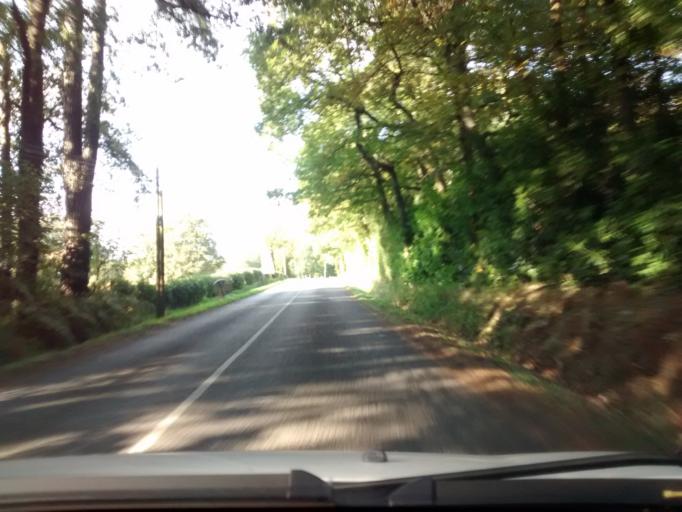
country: FR
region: Pays de la Loire
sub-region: Departement de la Loire-Atlantique
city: Sautron
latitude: 47.2715
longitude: -1.6714
